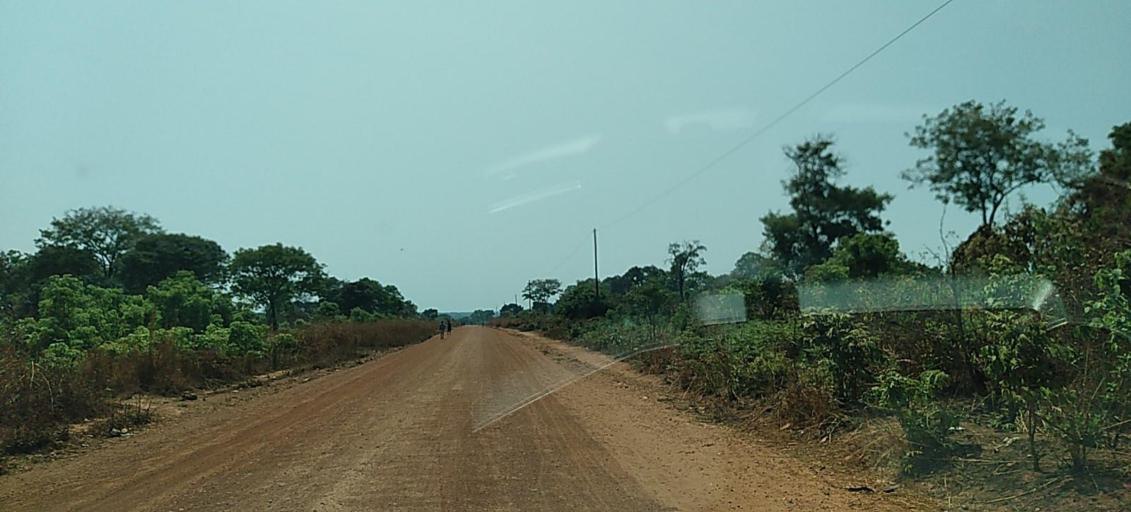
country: ZM
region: North-Western
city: Kansanshi
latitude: -11.9972
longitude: 26.6074
